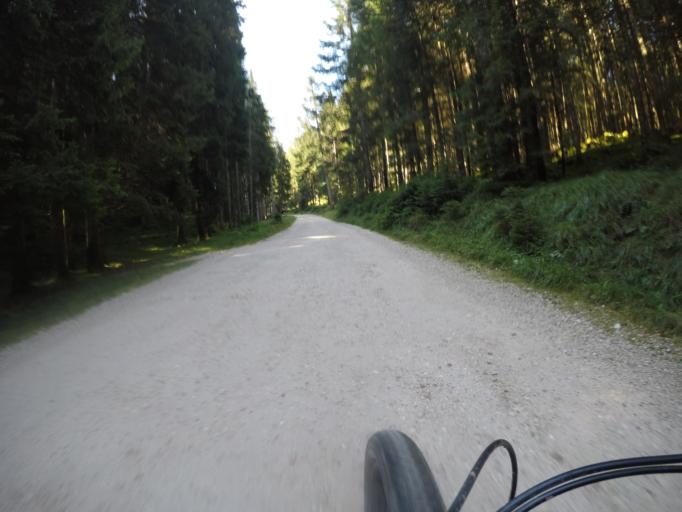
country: IT
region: Veneto
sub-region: Provincia di Vicenza
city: Asiago
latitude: 45.8515
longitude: 11.5272
